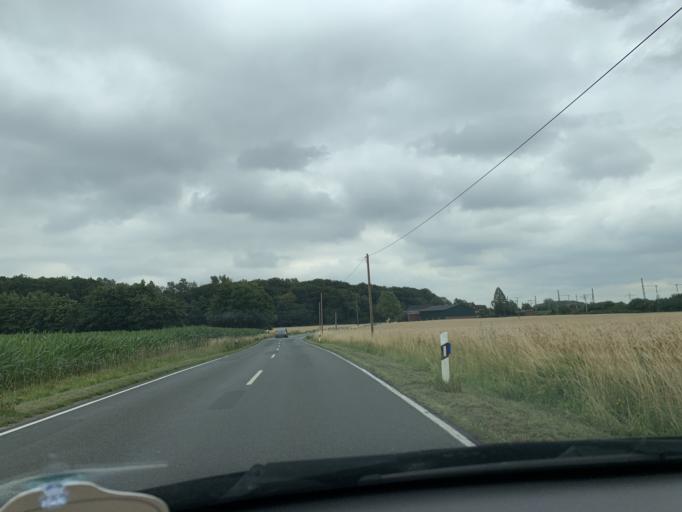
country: DE
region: North Rhine-Westphalia
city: Oelde
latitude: 51.8227
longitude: 8.0946
